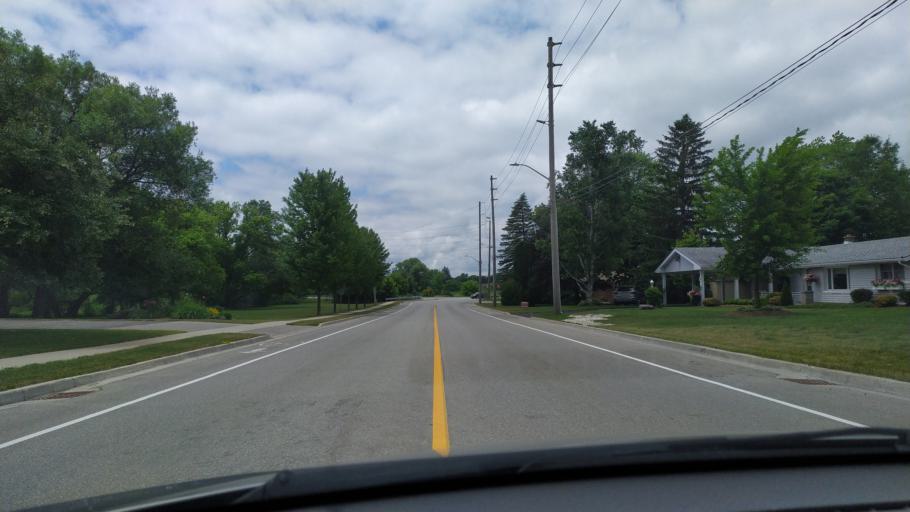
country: CA
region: Ontario
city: Stratford
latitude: 43.3893
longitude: -80.9657
